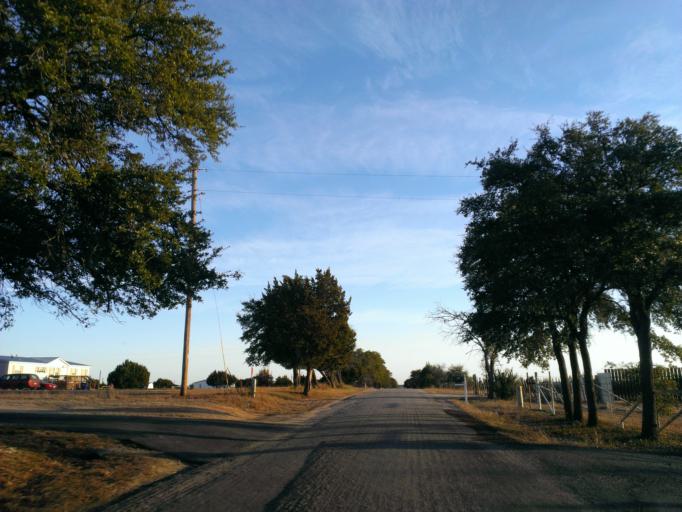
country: US
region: Texas
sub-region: Burnet County
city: Bertram
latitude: 30.7291
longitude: -98.0818
